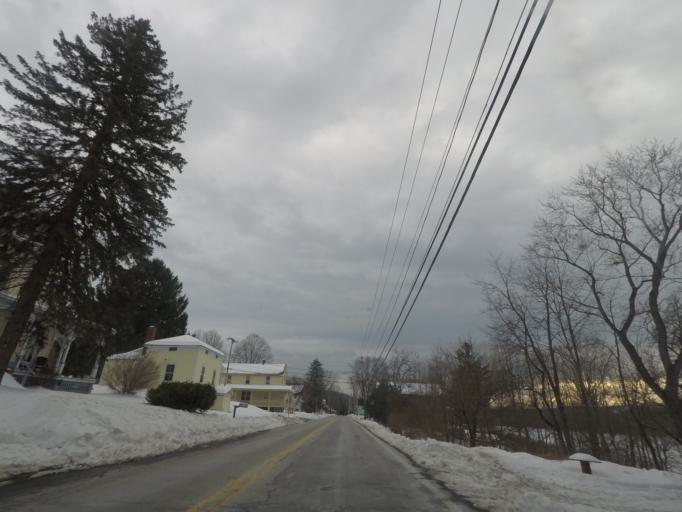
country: US
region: New York
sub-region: Rensselaer County
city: Castleton-on-Hudson
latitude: 42.4801
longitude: -73.7701
